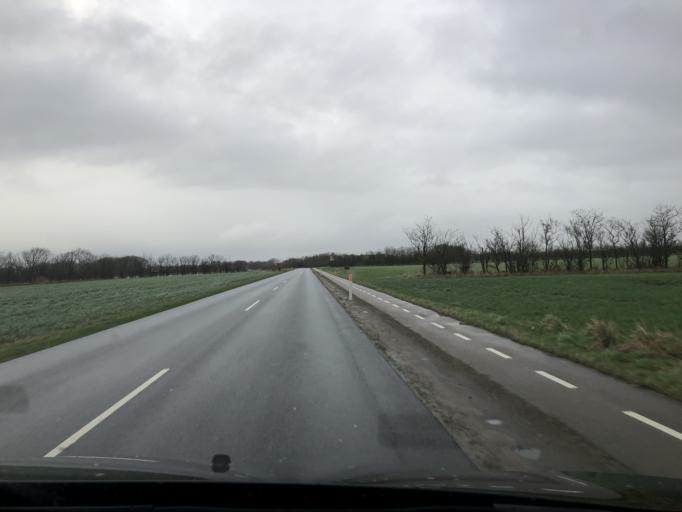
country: DK
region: Central Jutland
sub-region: Ringkobing-Skjern Kommune
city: Skjern
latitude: 55.9475
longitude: 8.4582
